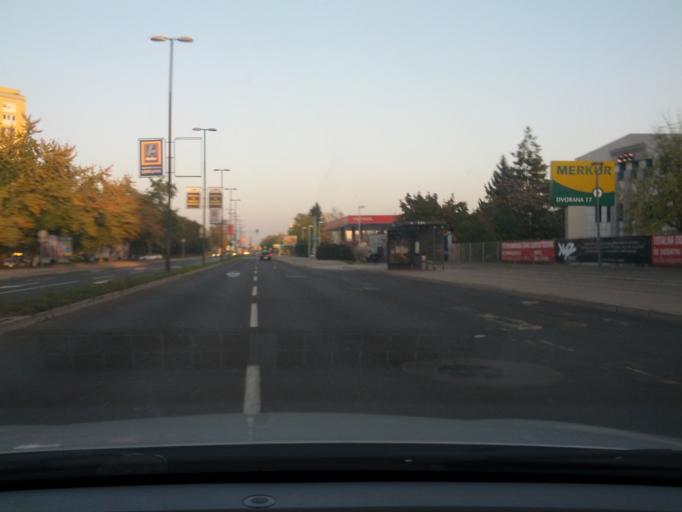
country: SI
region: Ljubljana
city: Ljubljana
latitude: 46.0692
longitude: 14.5409
